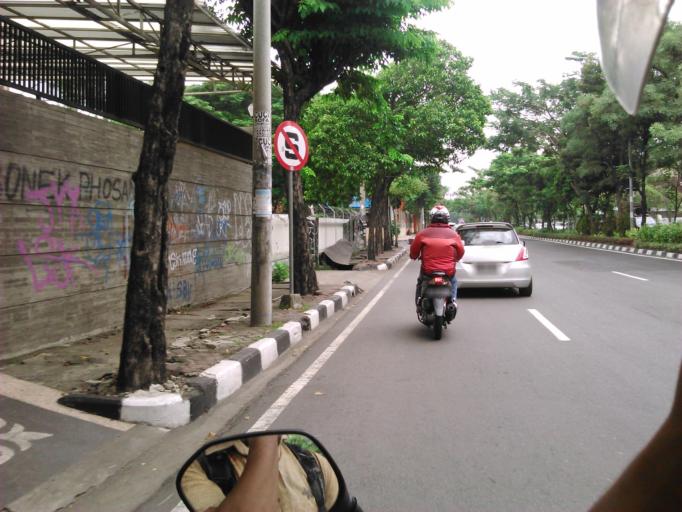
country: ID
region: East Java
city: Pacarkeling
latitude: -7.2586
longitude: 112.7509
